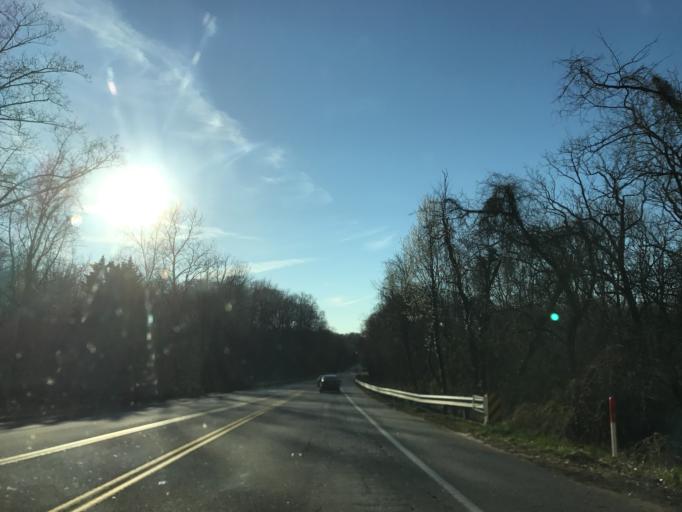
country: US
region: Maryland
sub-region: Anne Arundel County
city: Cape Saint Claire
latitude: 39.0361
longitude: -76.4646
